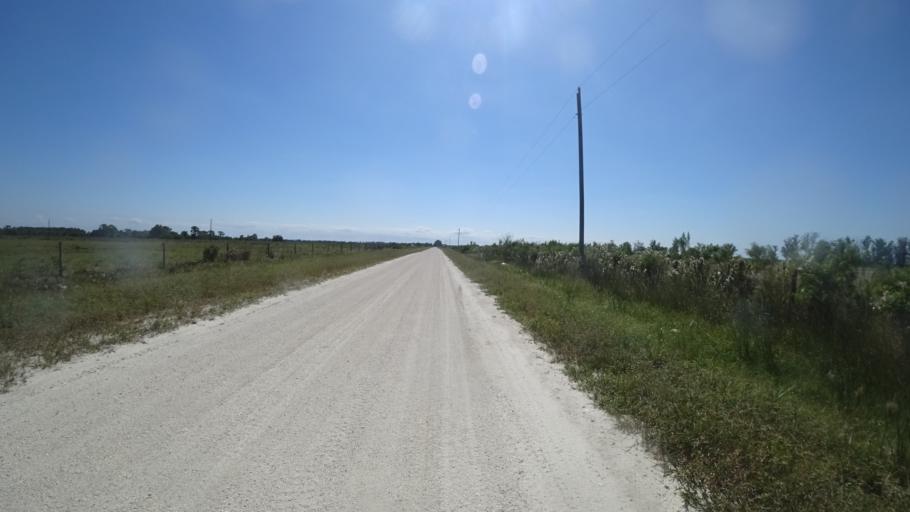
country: US
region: Florida
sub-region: DeSoto County
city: Arcadia
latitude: 27.3378
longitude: -82.0806
